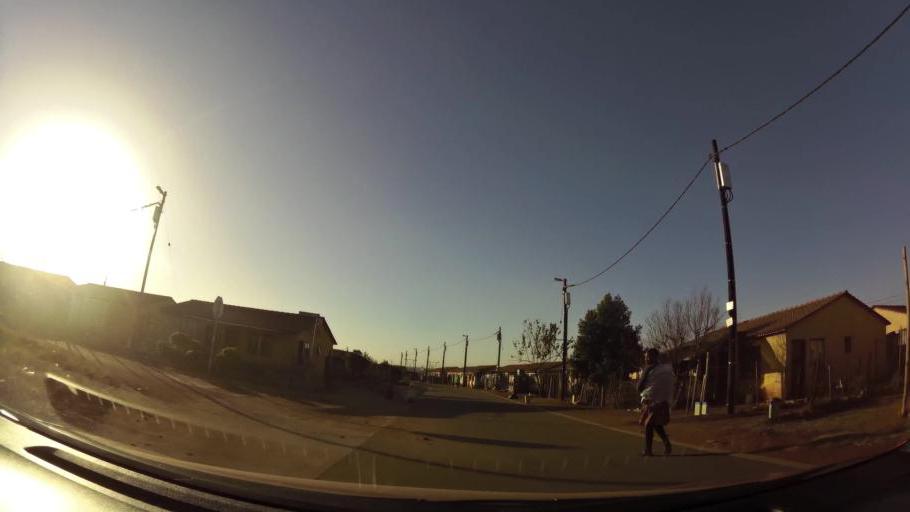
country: ZA
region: Gauteng
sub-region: City of Tshwane Metropolitan Municipality
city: Mabopane
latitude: -25.6003
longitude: 28.1057
